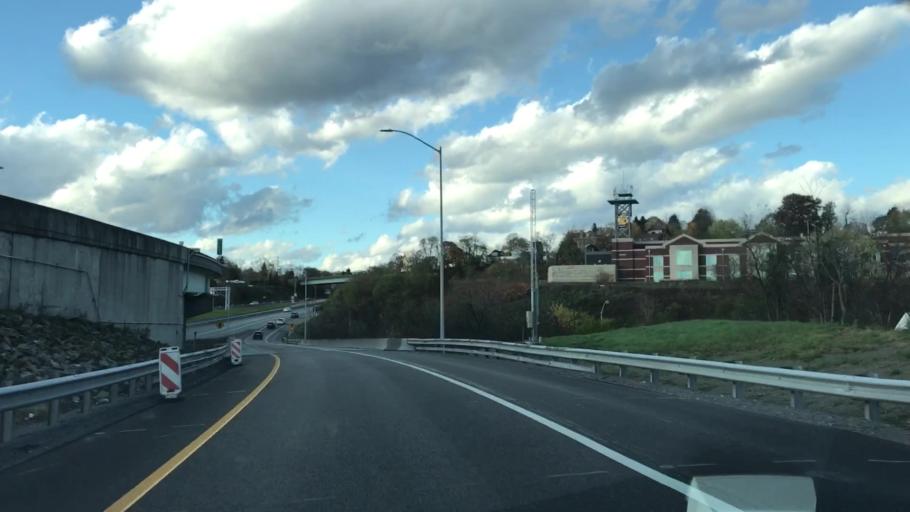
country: US
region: Pennsylvania
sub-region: Allegheny County
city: Millvale
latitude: 40.4933
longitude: -80.0102
